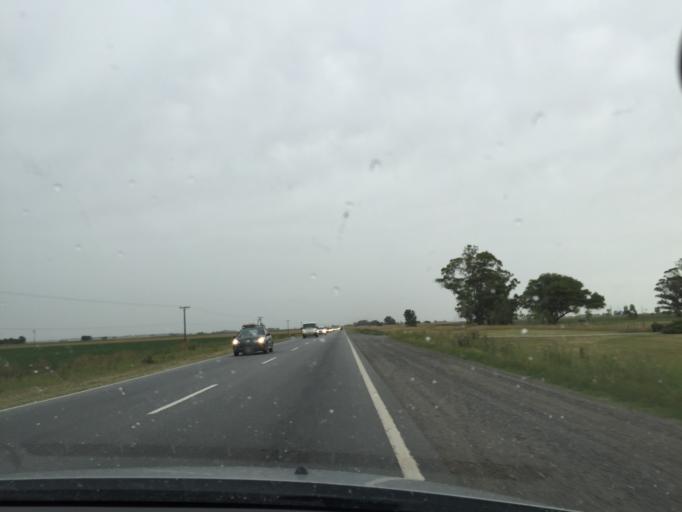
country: AR
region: Buenos Aires
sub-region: Partido de Tandil
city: Tandil
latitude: -37.5556
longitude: -58.7964
